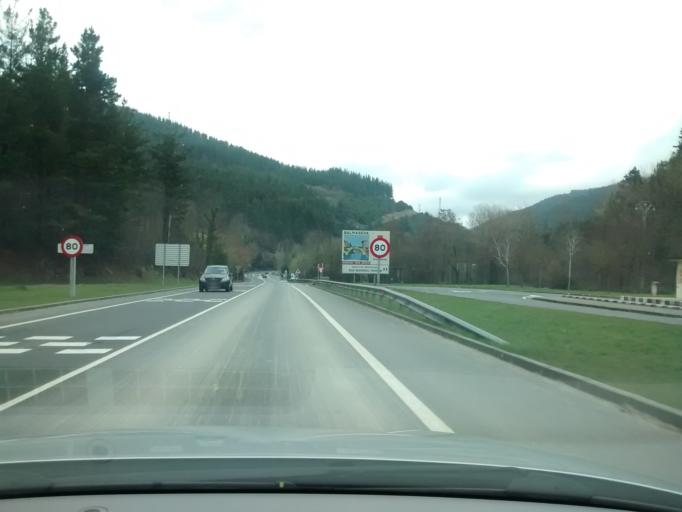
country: ES
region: Basque Country
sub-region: Bizkaia
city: Balmaseda
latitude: 43.1735
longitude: -3.2220
